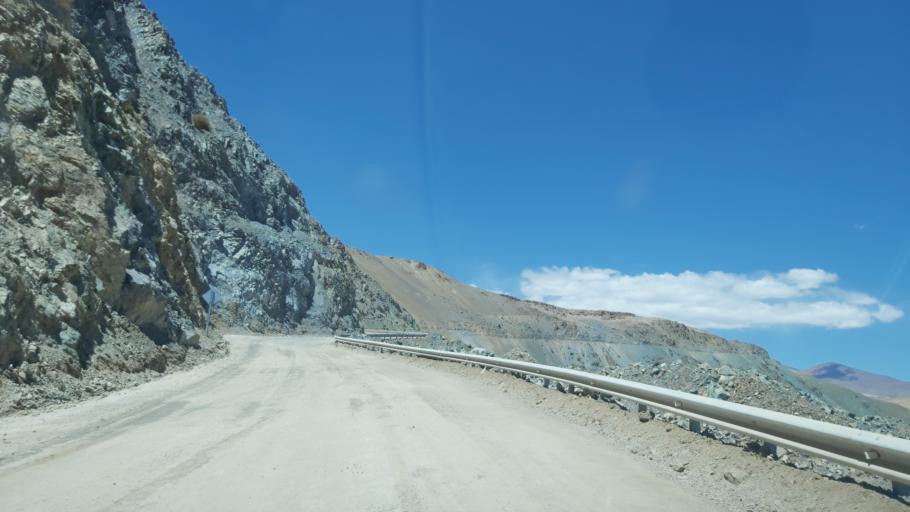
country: CL
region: Atacama
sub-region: Provincia de Chanaral
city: Diego de Almagro
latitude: -26.4562
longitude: -69.3139
